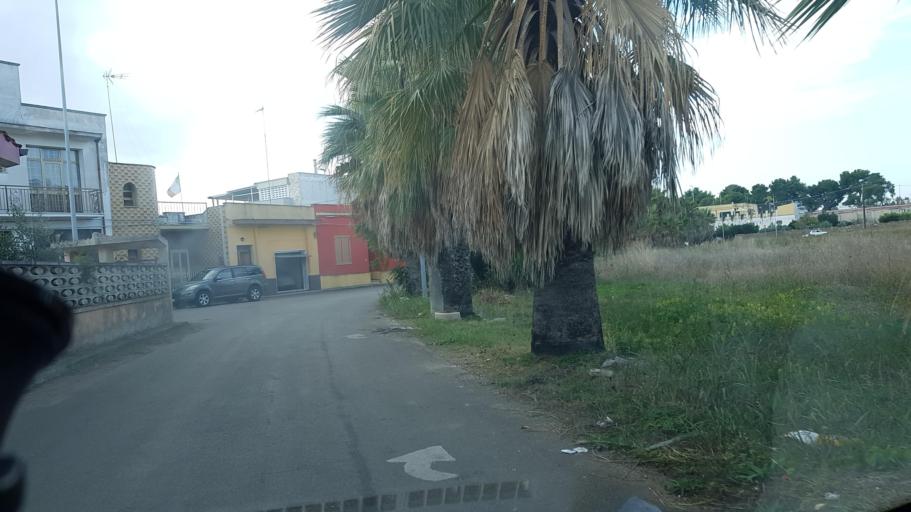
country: IT
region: Apulia
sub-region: Provincia di Brindisi
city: San Pietro Vernotico
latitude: 40.4913
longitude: 18.0033
